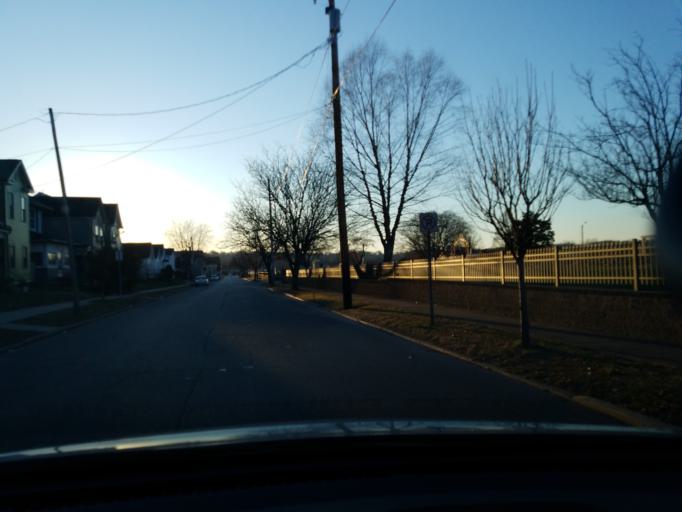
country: US
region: Indiana
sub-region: Floyd County
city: New Albany
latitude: 38.2911
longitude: -85.8185
